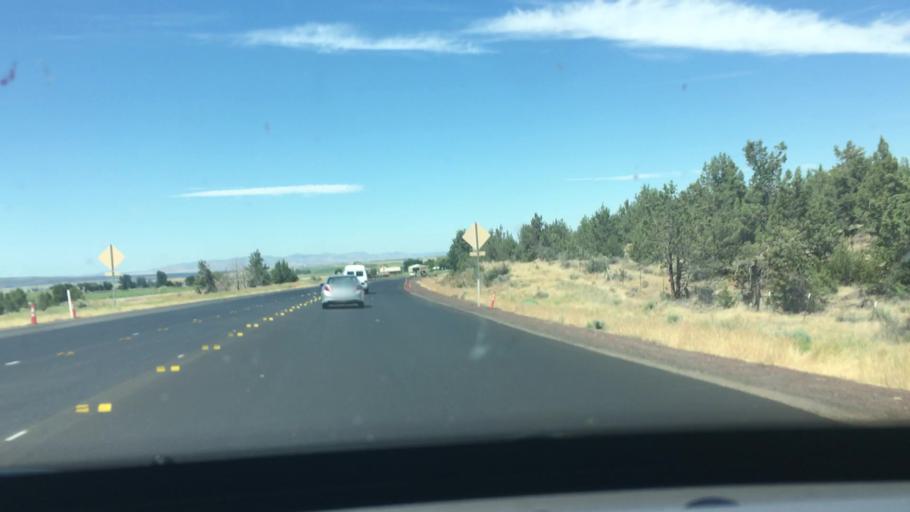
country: US
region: Oregon
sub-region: Jefferson County
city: Culver
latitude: 44.4933
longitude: -121.1930
